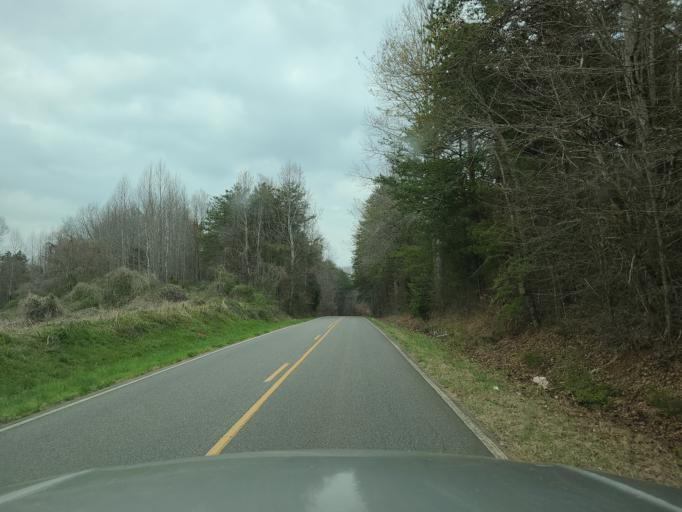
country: US
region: North Carolina
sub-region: Cleveland County
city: Shelby
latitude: 35.3299
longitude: -81.5340
